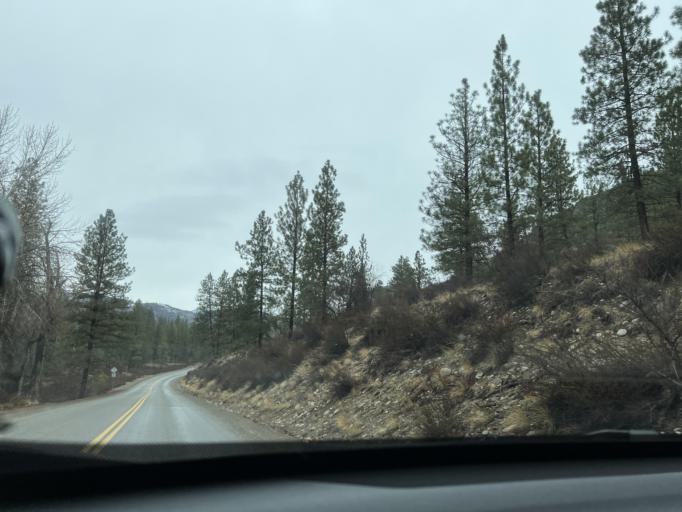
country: US
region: Washington
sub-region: Okanogan County
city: Brewster
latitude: 48.5307
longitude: -120.1802
